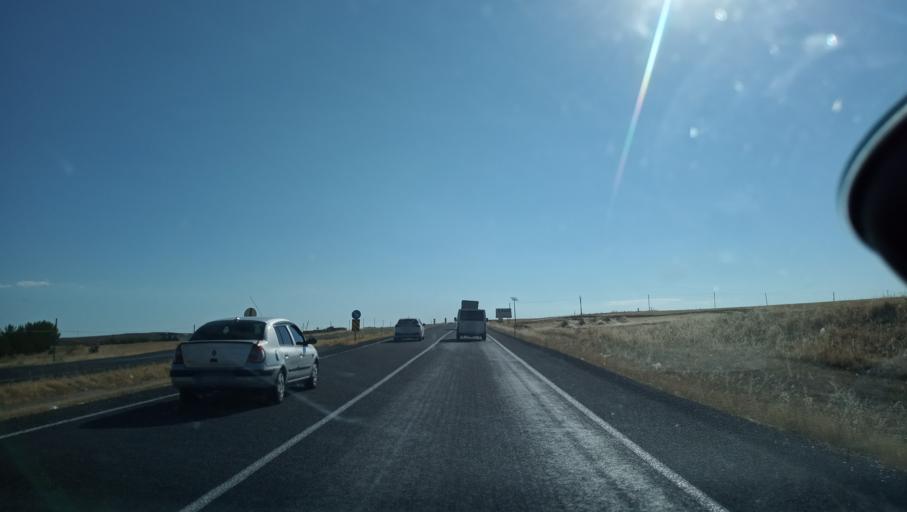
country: TR
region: Diyarbakir
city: Ambar
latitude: 37.9973
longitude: 40.4098
